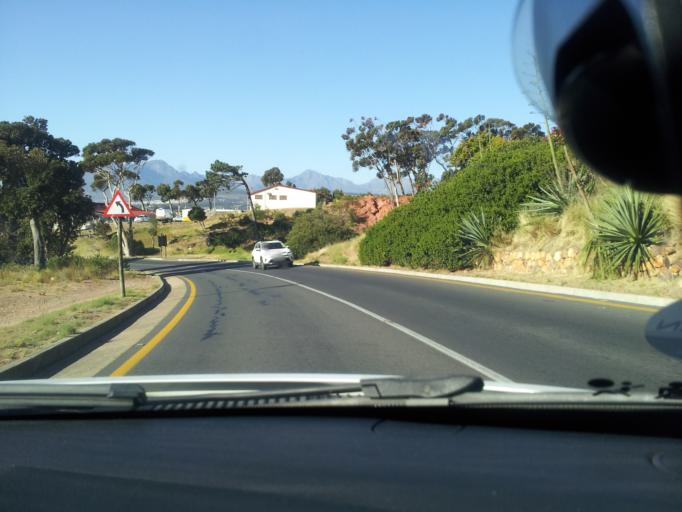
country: ZA
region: Western Cape
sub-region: Overberg District Municipality
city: Grabouw
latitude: -34.1600
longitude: 18.8718
